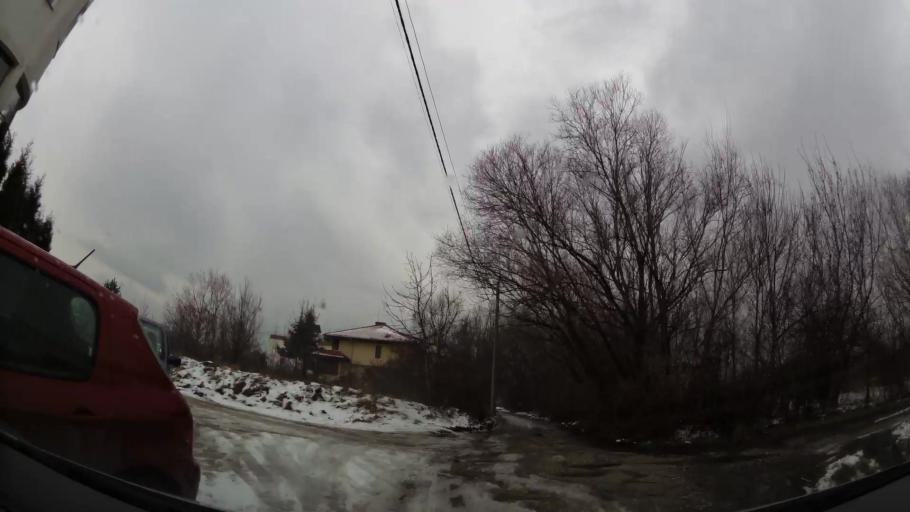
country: BG
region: Sofia-Capital
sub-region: Stolichna Obshtina
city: Sofia
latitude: 42.6527
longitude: 23.2985
